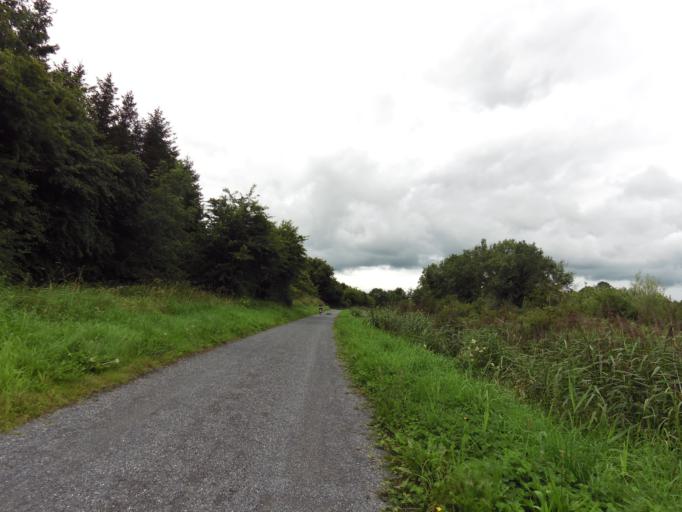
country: IE
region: Leinster
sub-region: An Iarmhi
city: An Muileann gCearr
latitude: 53.5200
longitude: -7.4399
